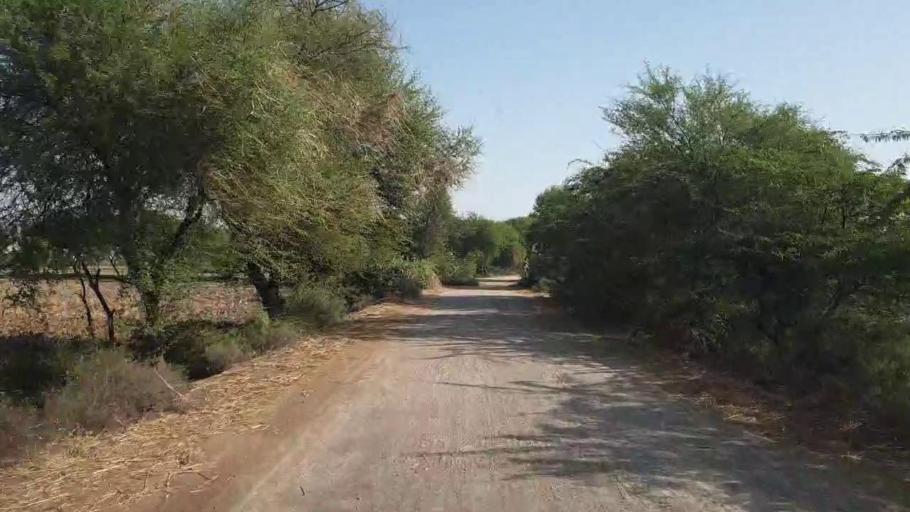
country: PK
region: Sindh
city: Matli
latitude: 25.0185
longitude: 68.7398
